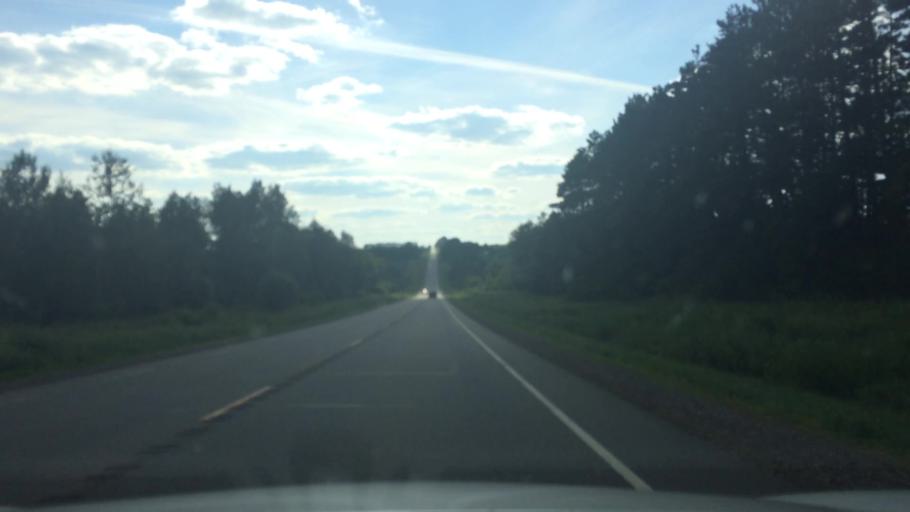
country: US
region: Wisconsin
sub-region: Lincoln County
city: Merrill
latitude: 45.1779
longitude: -89.5884
